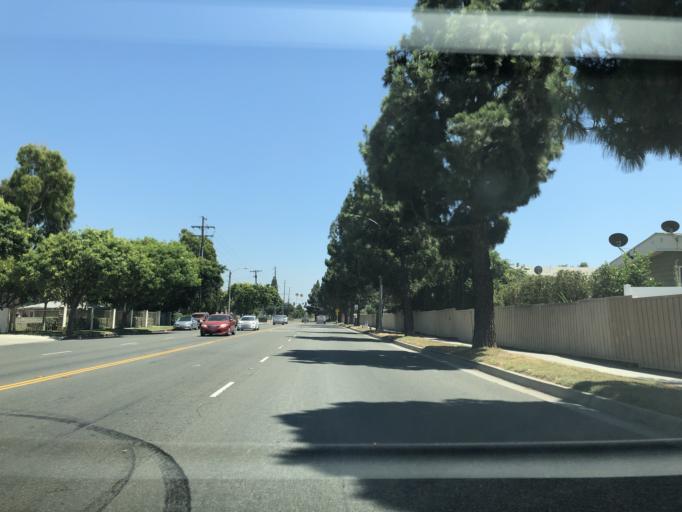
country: US
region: California
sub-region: Riverside County
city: Corona
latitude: 33.8754
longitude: -117.5913
